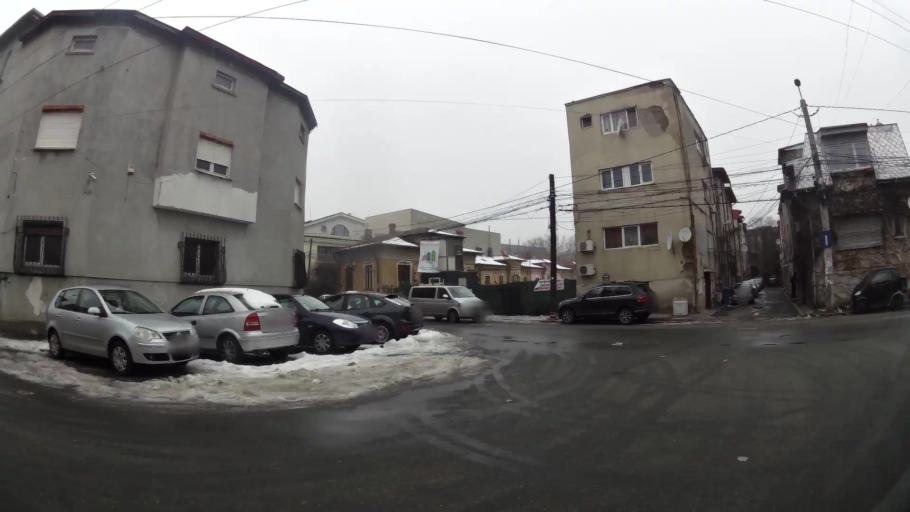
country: RO
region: Bucuresti
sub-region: Municipiul Bucuresti
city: Bucharest
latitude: 44.4435
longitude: 26.1250
